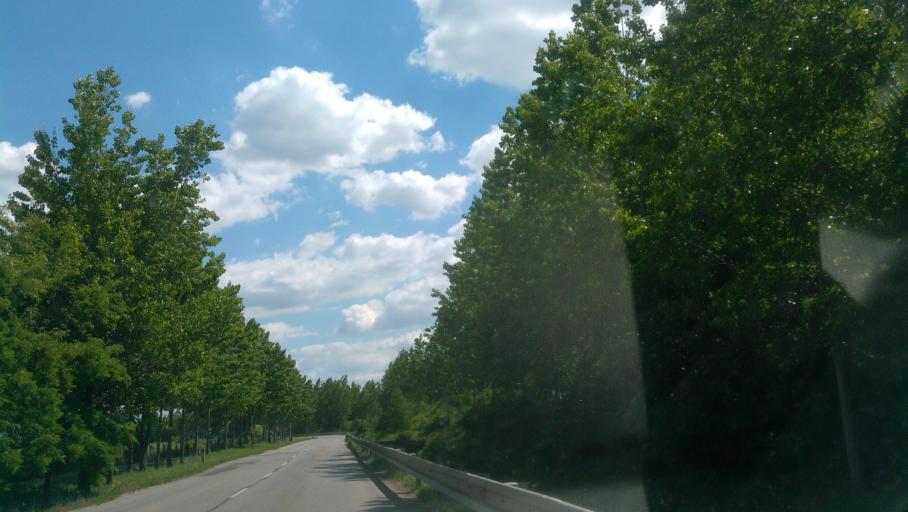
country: SK
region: Nitriansky
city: Kolarovo
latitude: 47.8999
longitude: 18.0053
